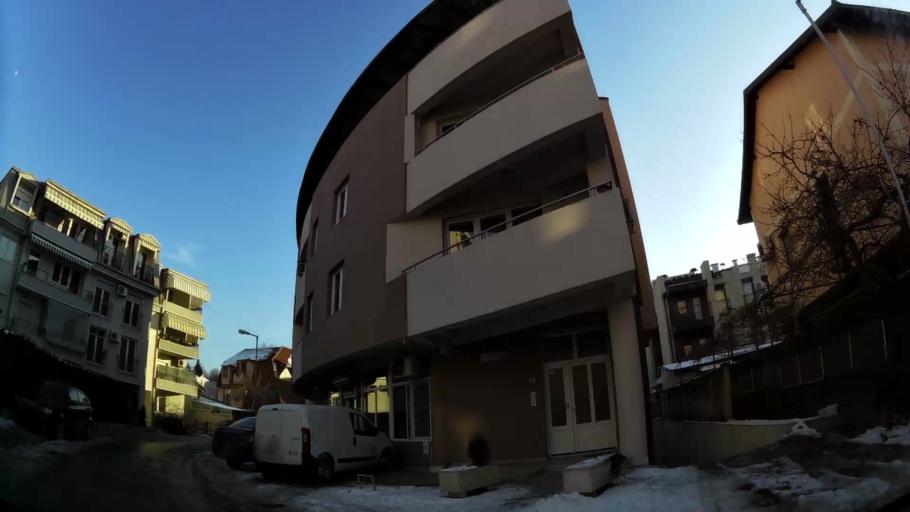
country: MK
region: Karpos
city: Skopje
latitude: 41.9945
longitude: 21.4054
